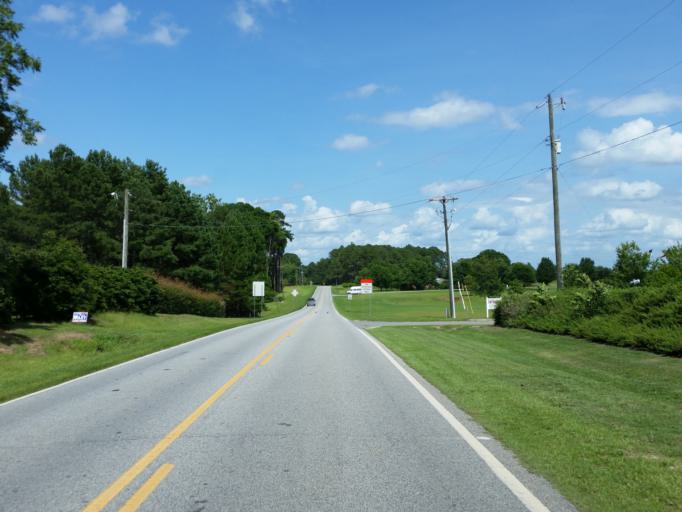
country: US
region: Georgia
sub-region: Tift County
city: Tifton
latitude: 31.5055
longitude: -83.5093
